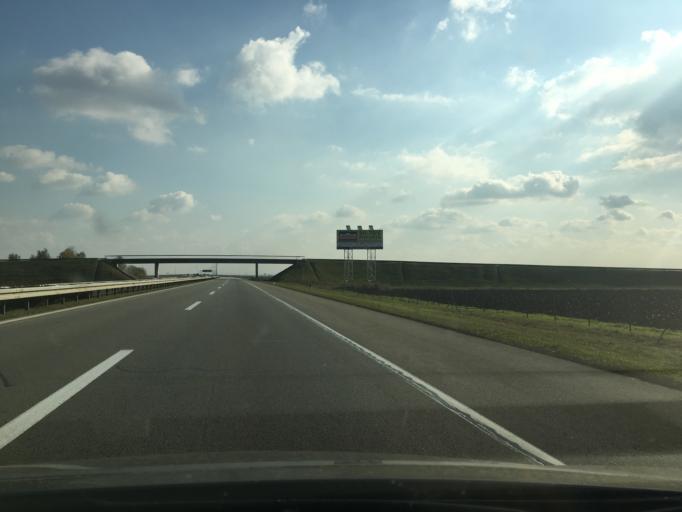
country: RS
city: Krcedin
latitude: 45.1031
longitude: 20.1104
